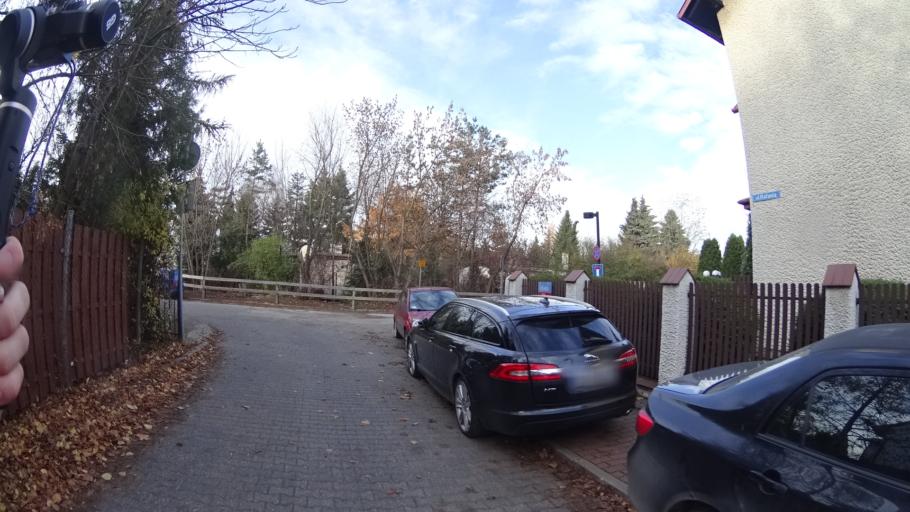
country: PL
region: Masovian Voivodeship
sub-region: Warszawa
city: Targowek
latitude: 52.2836
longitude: 21.0612
